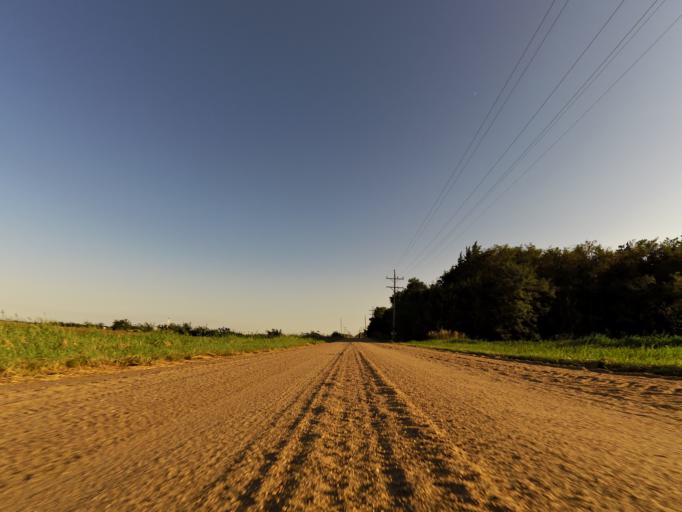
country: US
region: Kansas
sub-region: Reno County
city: South Hutchinson
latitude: 38.0062
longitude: -98.0319
